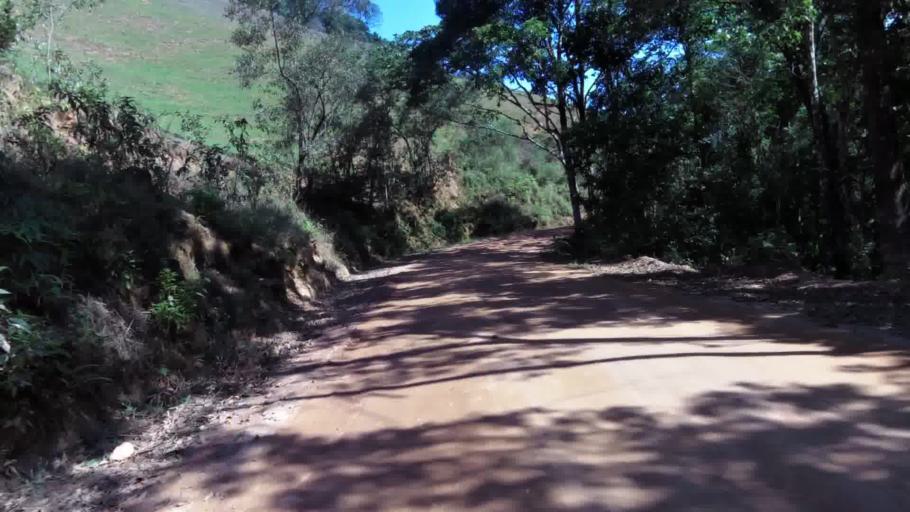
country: BR
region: Espirito Santo
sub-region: Alfredo Chaves
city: Alfredo Chaves
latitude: -20.5739
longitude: -40.7890
